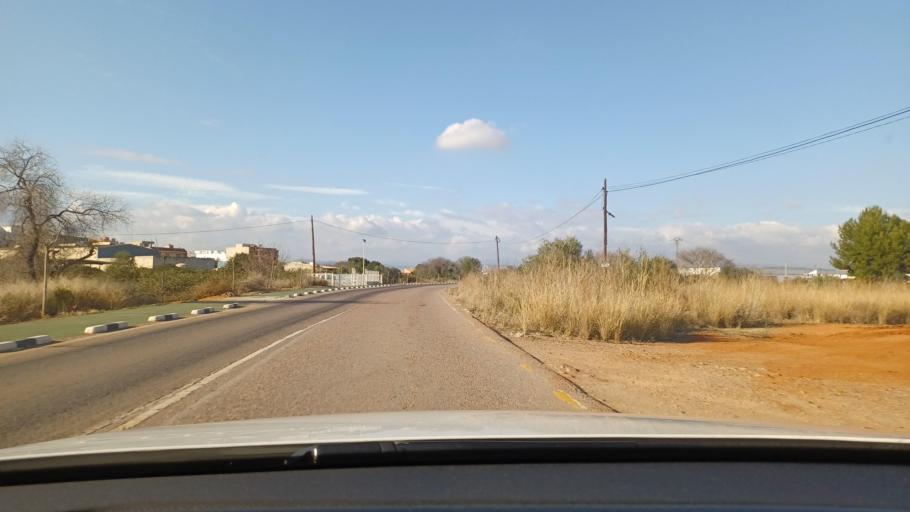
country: ES
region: Valencia
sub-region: Provincia de Castello
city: Betxi
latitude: 39.9289
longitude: -0.1936
